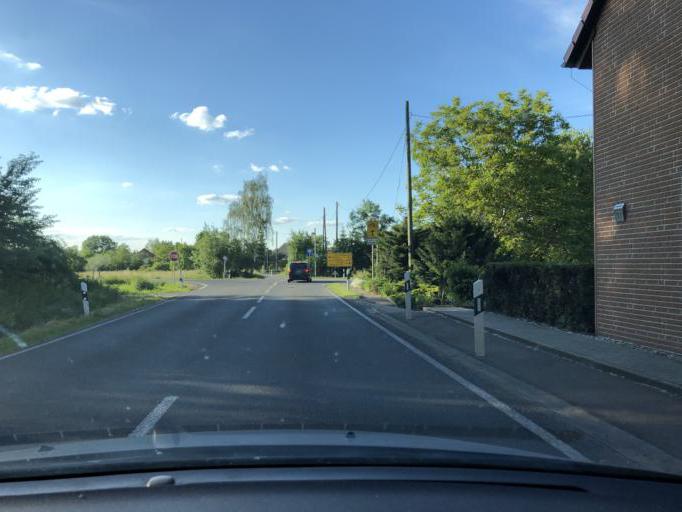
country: DE
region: Saxony
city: Groitzsch
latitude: 51.1441
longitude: 12.2917
